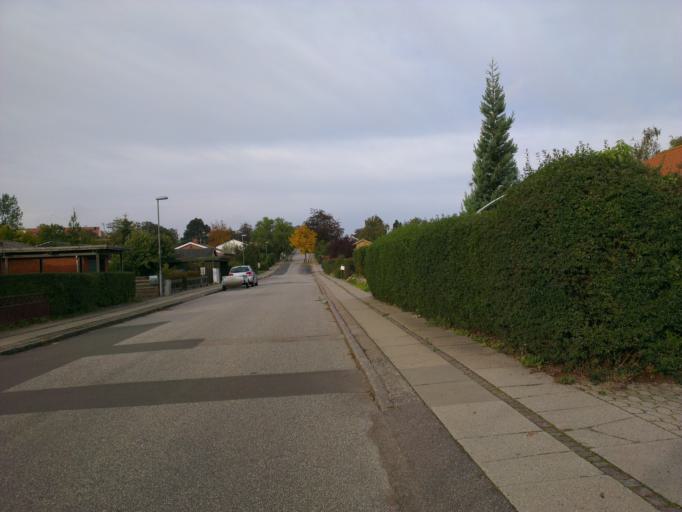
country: DK
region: Capital Region
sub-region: Frederikssund Kommune
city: Frederikssund
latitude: 55.8455
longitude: 12.0584
